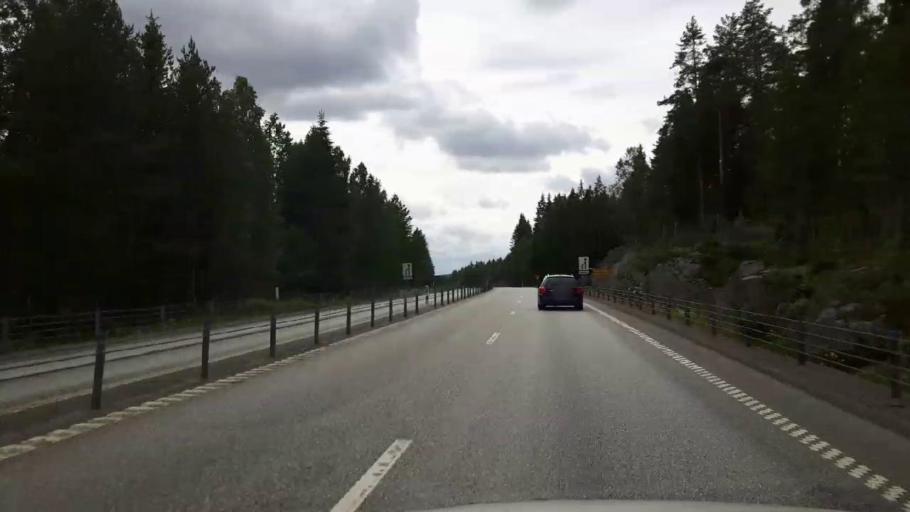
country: SE
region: Vaestmanland
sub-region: Fagersta Kommun
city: Fagersta
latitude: 60.0293
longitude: 15.8009
